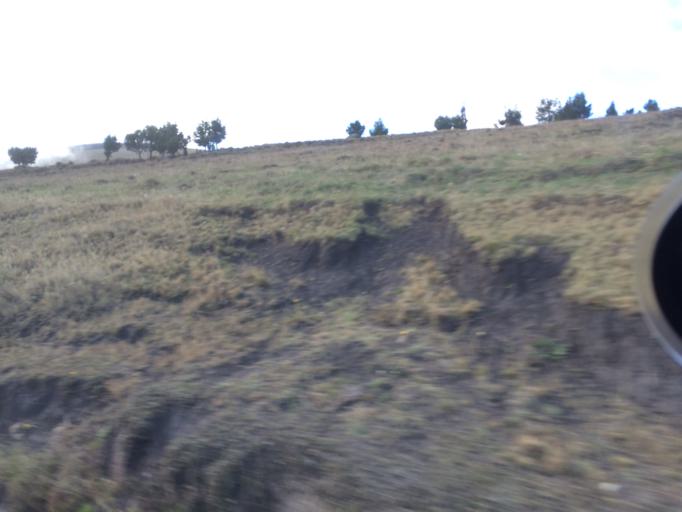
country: EC
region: Chimborazo
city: Alausi
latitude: -2.2488
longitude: -78.6632
